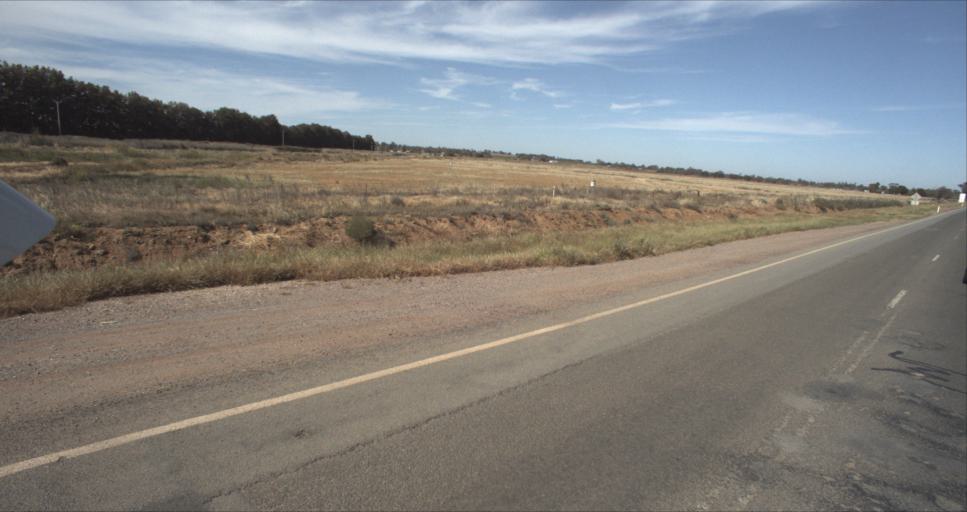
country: AU
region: New South Wales
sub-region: Leeton
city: Leeton
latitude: -34.5564
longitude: 146.4496
